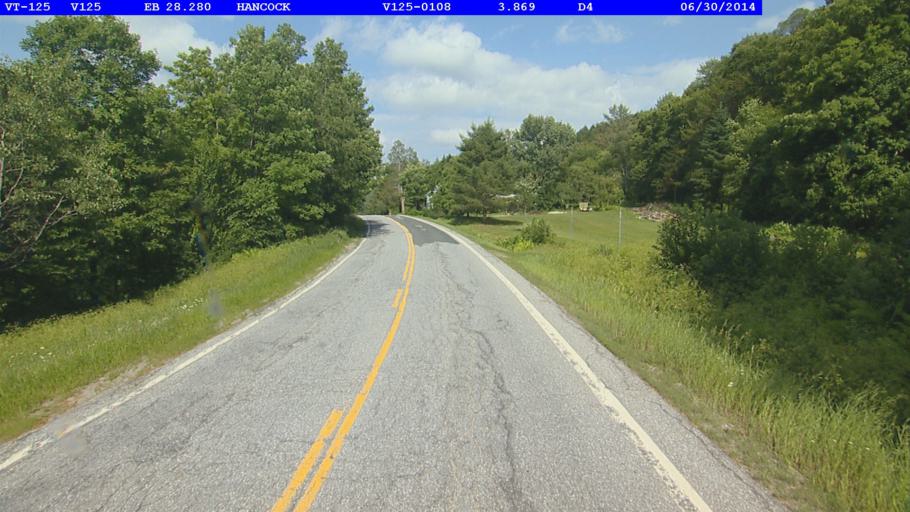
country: US
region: Vermont
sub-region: Rutland County
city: Brandon
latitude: 43.9275
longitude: -72.9052
